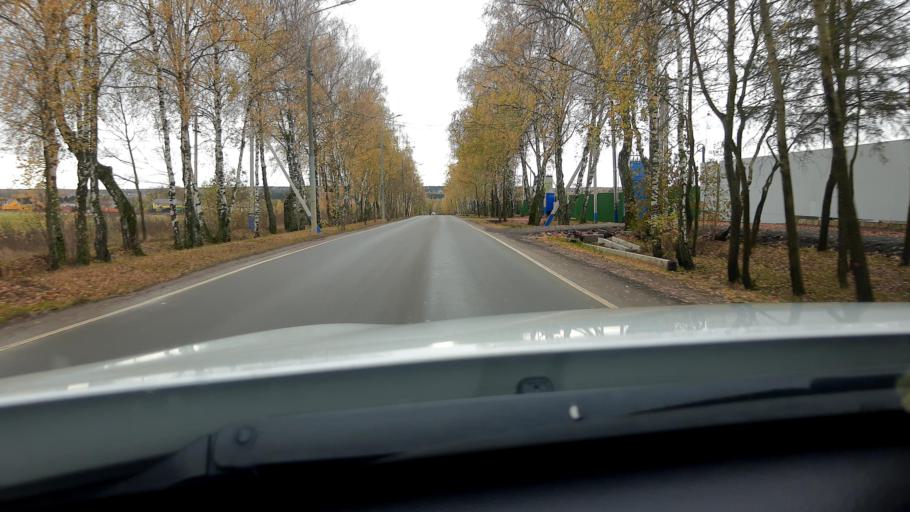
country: RU
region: Moskovskaya
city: Annino
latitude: 55.5715
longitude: 37.2370
